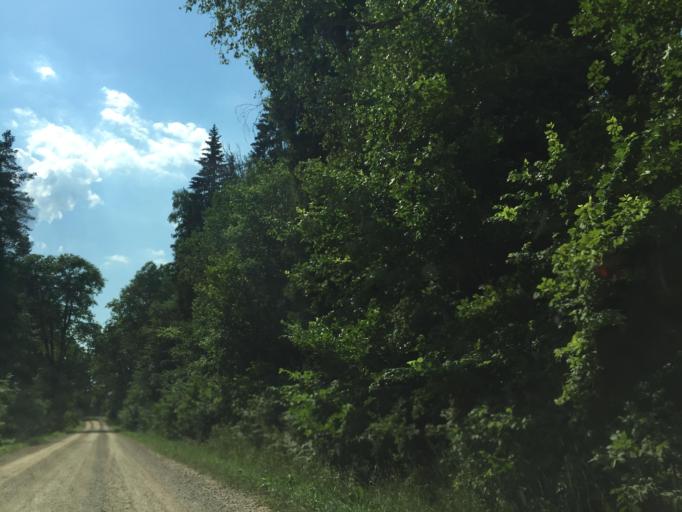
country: LV
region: Pargaujas
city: Stalbe
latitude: 57.3650
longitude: 25.0984
